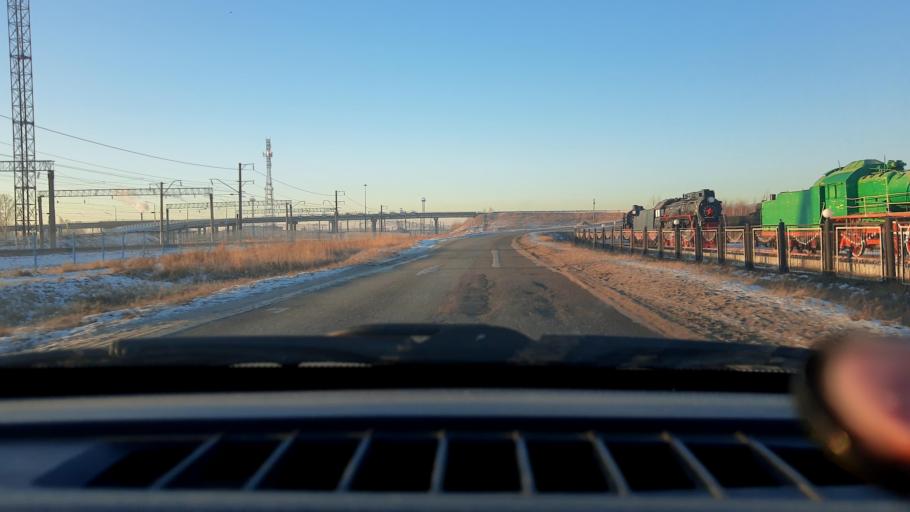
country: RU
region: Nizjnij Novgorod
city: Gorbatovka
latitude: 56.2834
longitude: 43.8454
